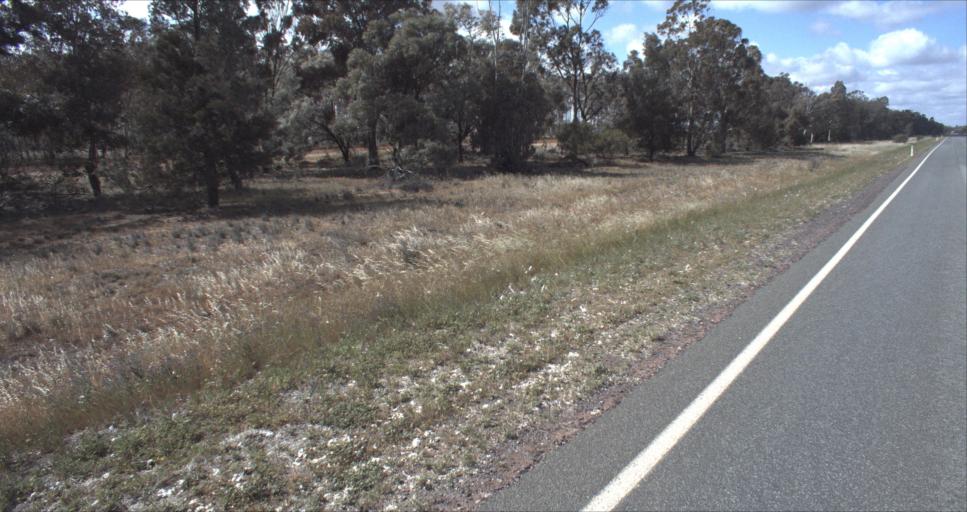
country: AU
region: New South Wales
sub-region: Murrumbidgee Shire
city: Darlington Point
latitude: -34.5847
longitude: 146.1645
